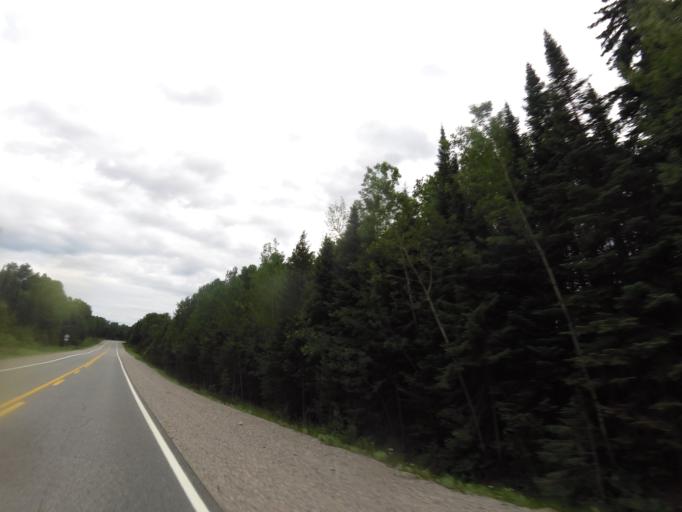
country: CA
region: Quebec
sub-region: Abitibi-Temiscamingue
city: Amos
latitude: 48.9483
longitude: -77.9528
